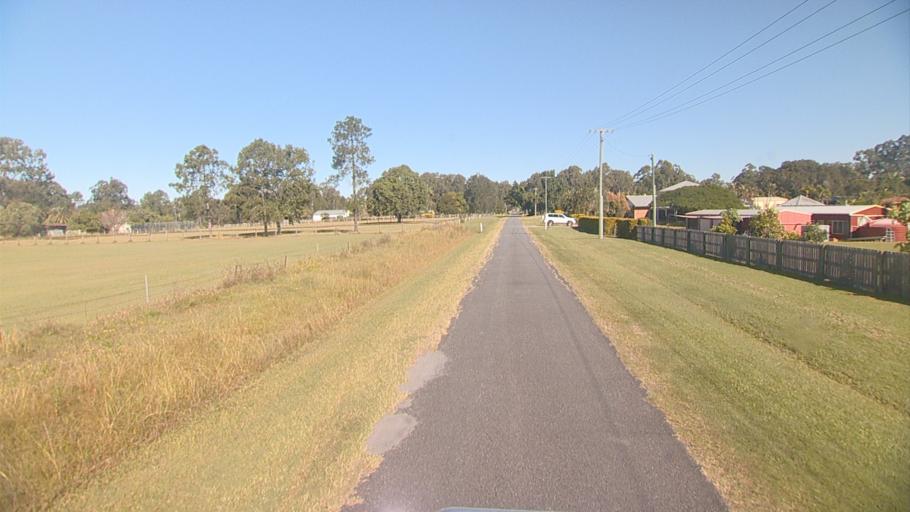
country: AU
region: Queensland
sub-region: Logan
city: Waterford West
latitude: -27.7169
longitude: 153.1264
